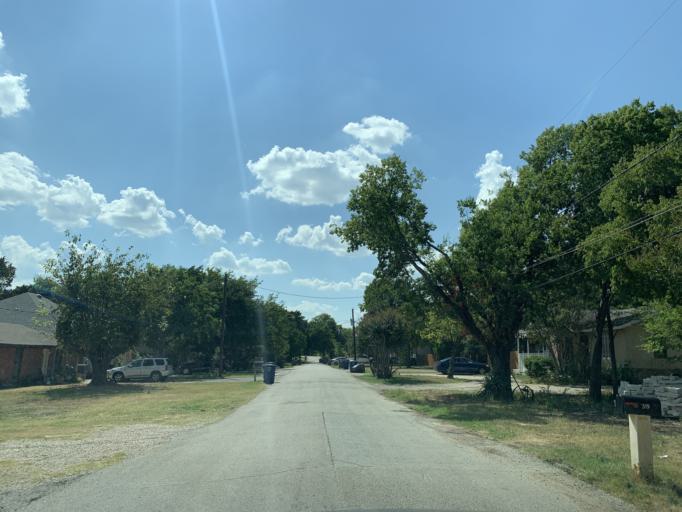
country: US
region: Texas
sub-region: Dallas County
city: DeSoto
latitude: 32.6673
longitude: -96.8187
